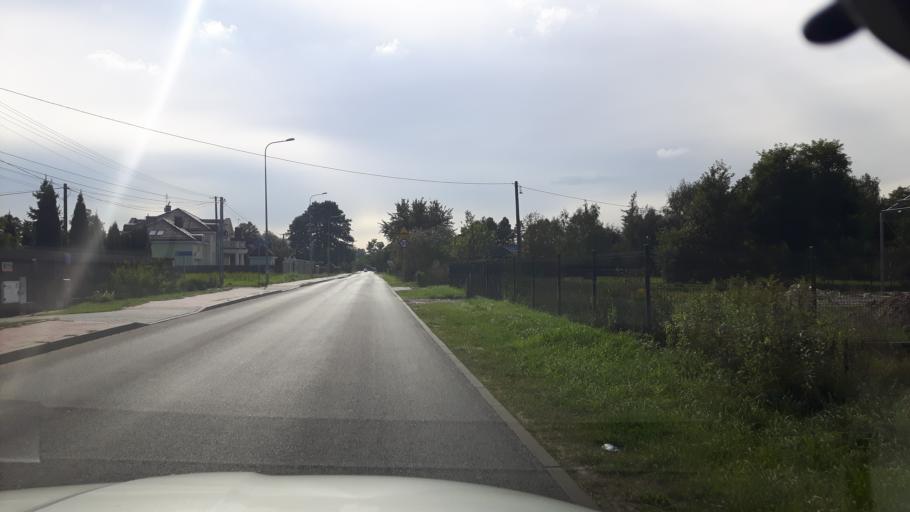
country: PL
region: Masovian Voivodeship
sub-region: Powiat legionowski
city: Stanislawow Pierwszy
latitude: 52.3715
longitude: 21.0396
